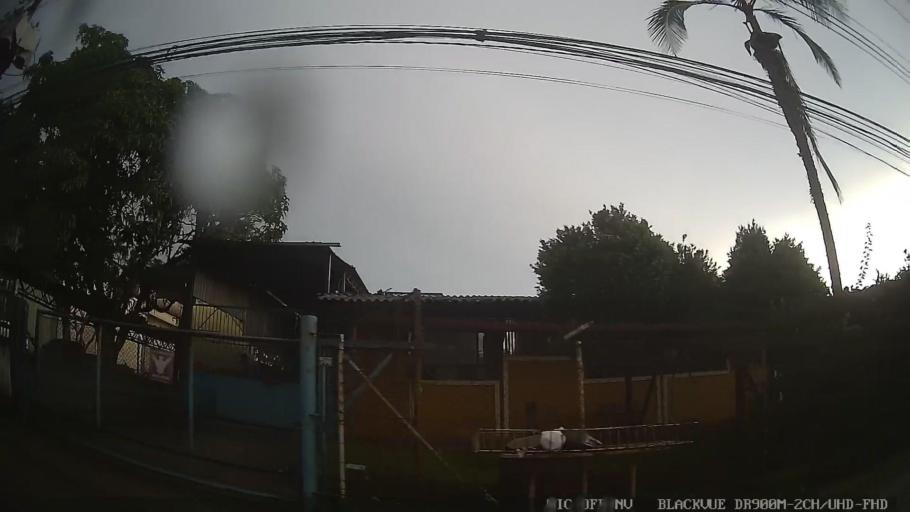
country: BR
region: Sao Paulo
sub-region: Ribeirao Pires
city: Ribeirao Pires
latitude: -23.7032
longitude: -46.3952
